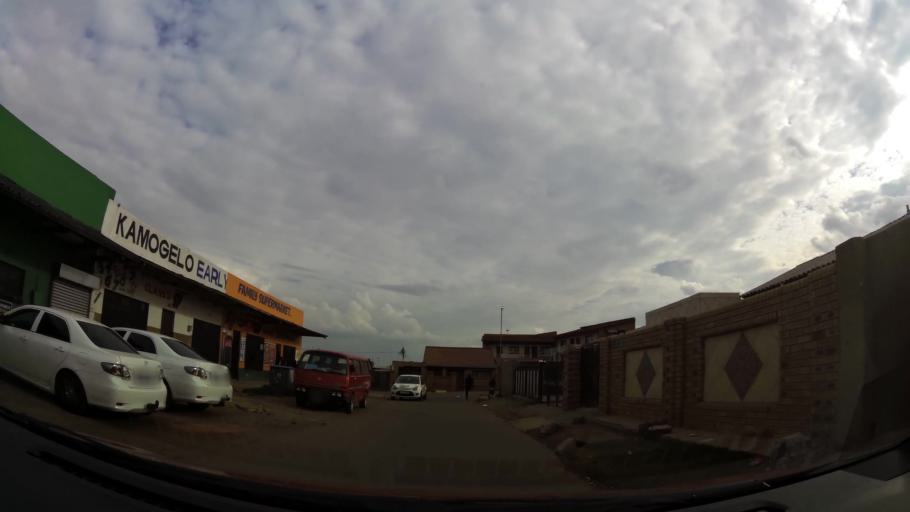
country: ZA
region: Gauteng
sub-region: City of Johannesburg Metropolitan Municipality
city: Soweto
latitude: -26.2463
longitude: 27.8380
